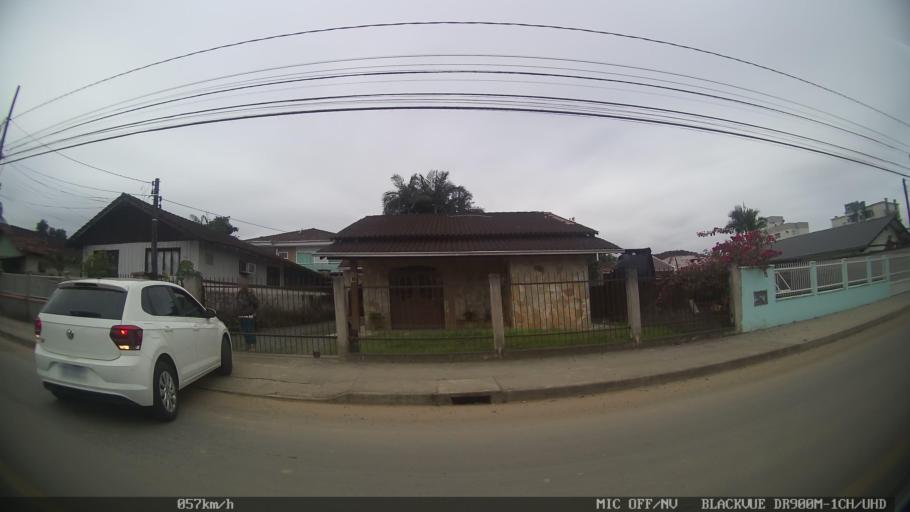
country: BR
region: Santa Catarina
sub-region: Joinville
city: Joinville
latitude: -26.2955
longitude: -48.9019
